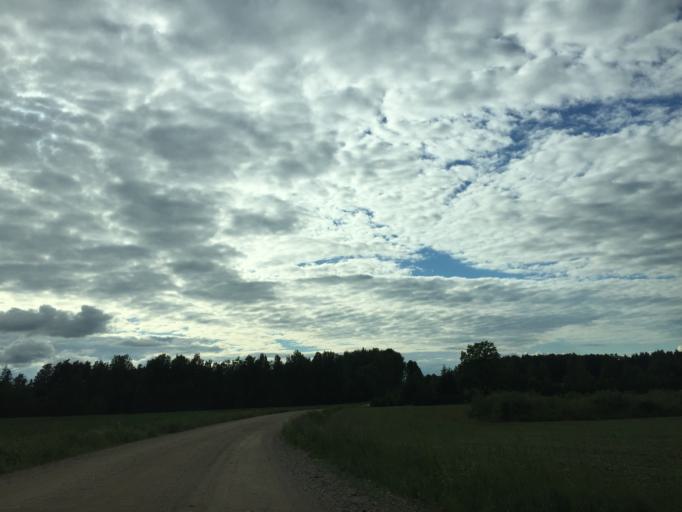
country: LV
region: Amatas Novads
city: Drabesi
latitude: 57.2514
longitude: 25.1756
